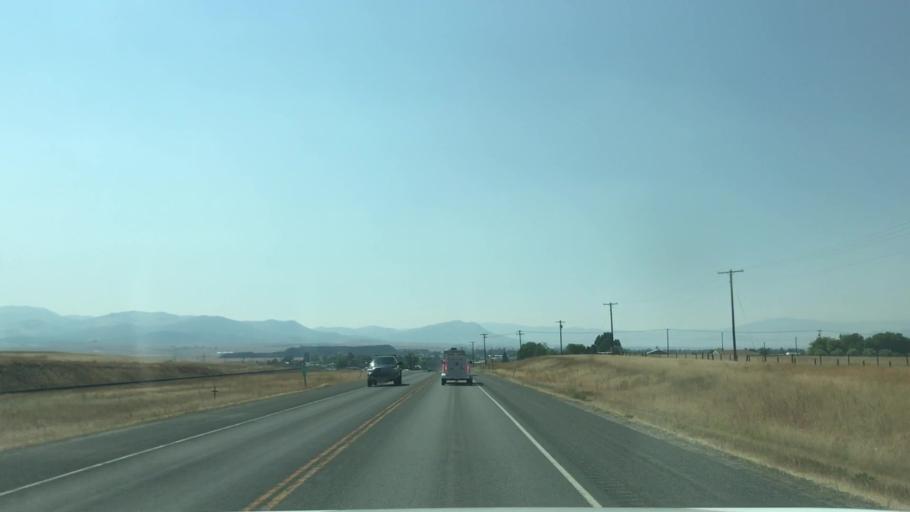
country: US
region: Montana
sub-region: Lewis and Clark County
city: East Helena
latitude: 46.5876
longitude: -111.8850
